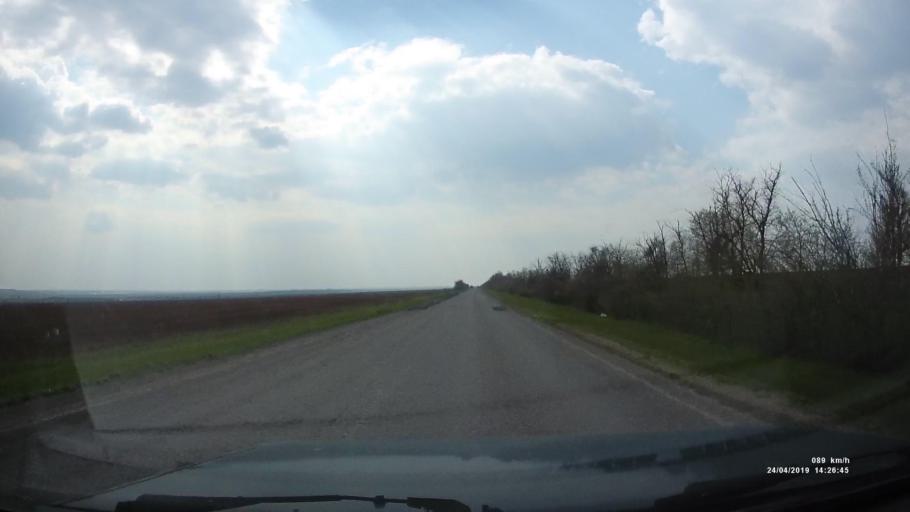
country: RU
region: Kalmykiya
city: Arshan'
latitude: 46.3342
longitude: 44.0561
